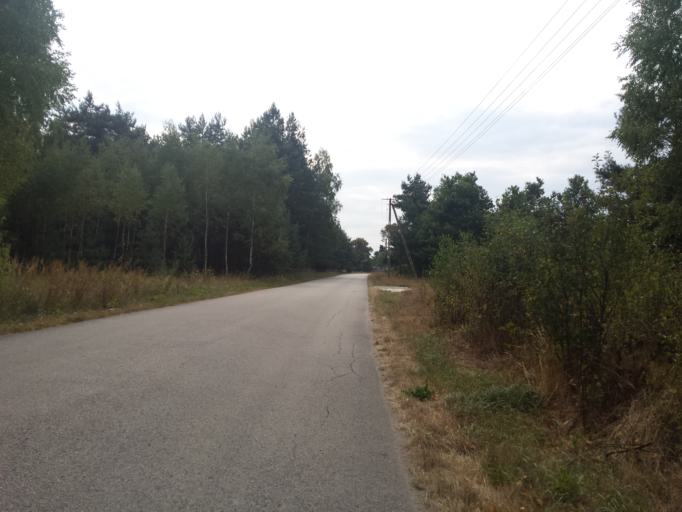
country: PL
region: Swietokrzyskie
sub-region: Powiat kielecki
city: Rakow
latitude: 50.6672
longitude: 21.1211
